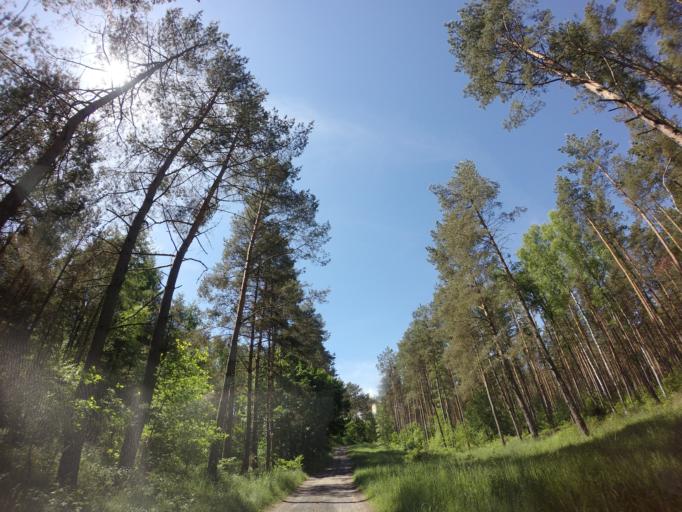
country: PL
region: West Pomeranian Voivodeship
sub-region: Powiat choszczenski
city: Drawno
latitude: 53.2929
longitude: 15.6889
